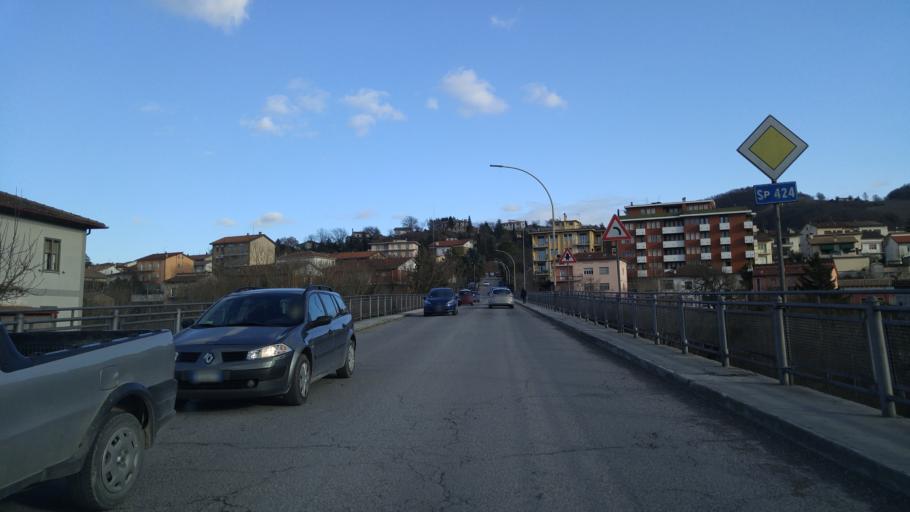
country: IT
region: The Marches
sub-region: Provincia di Pesaro e Urbino
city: Cagli
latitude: 43.5459
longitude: 12.6505
